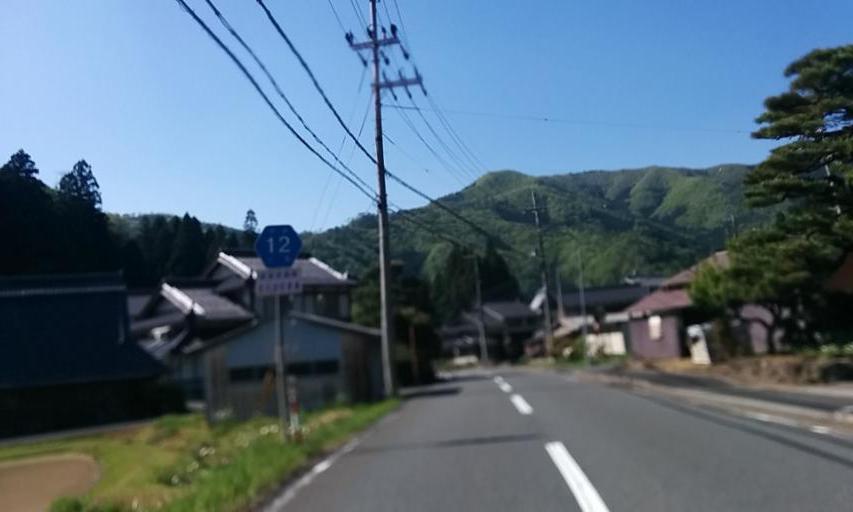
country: JP
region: Kyoto
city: Ayabe
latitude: 35.2615
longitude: 135.4526
